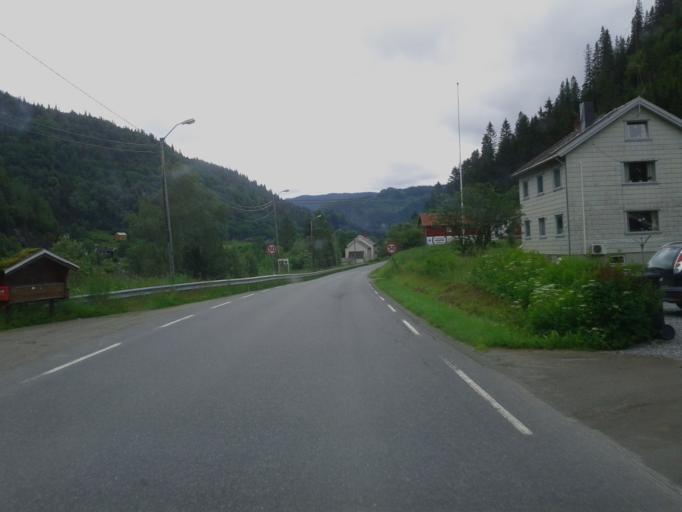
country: NO
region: Sor-Trondelag
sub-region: Midtre Gauldal
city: Storen
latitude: 63.0108
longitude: 10.4471
